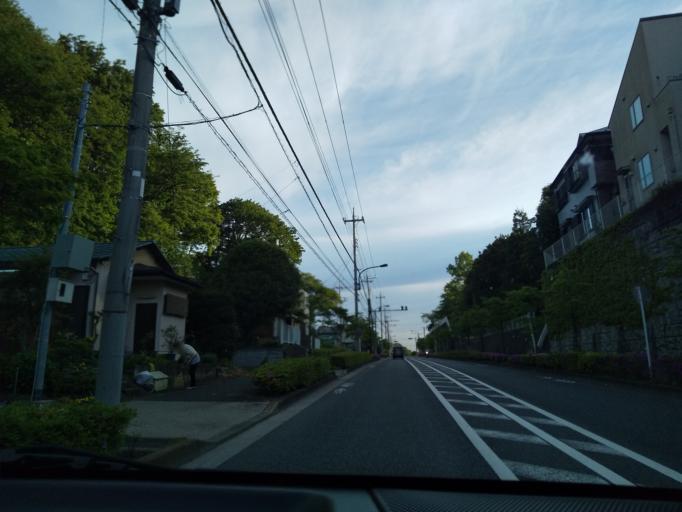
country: JP
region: Tokyo
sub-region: Machida-shi
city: Machida
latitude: 35.5663
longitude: 139.4533
